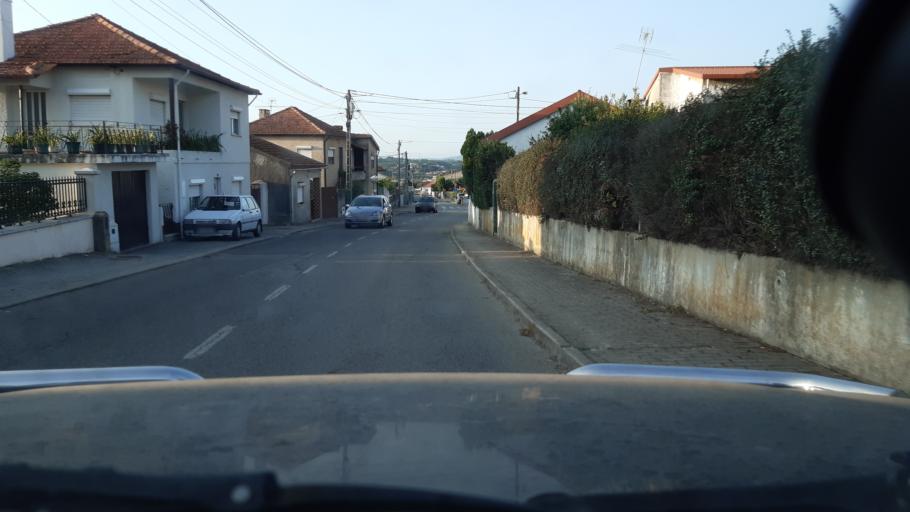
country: PT
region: Aveiro
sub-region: Agueda
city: Agueda
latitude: 40.5540
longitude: -8.4334
